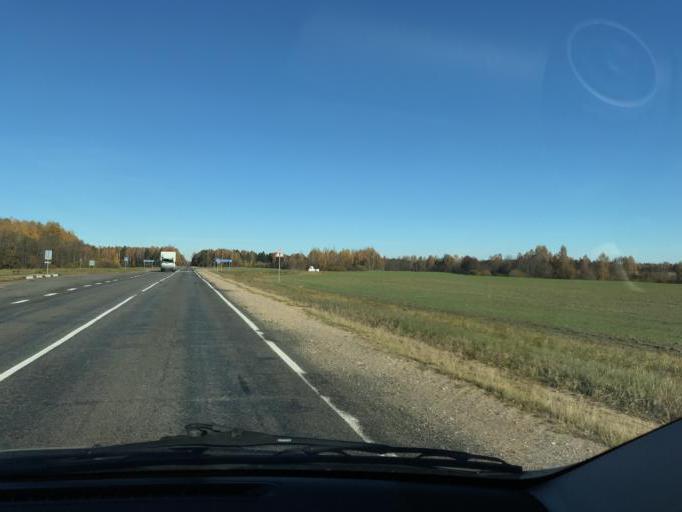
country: BY
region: Vitebsk
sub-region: Ushatski Rayon
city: Ushachy
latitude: 55.0848
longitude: 28.7558
